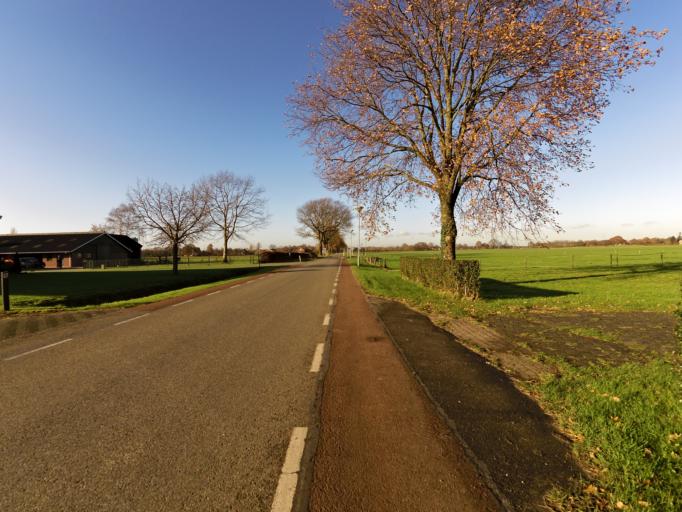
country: NL
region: Gelderland
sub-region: Gemeente Montferland
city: s-Heerenberg
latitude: 51.9257
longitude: 6.1847
